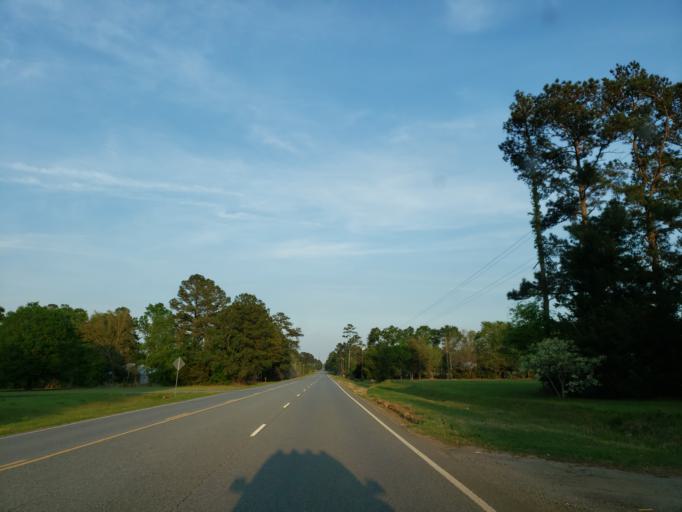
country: US
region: Georgia
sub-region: Lowndes County
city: Hahira
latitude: 30.9954
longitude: -83.4235
